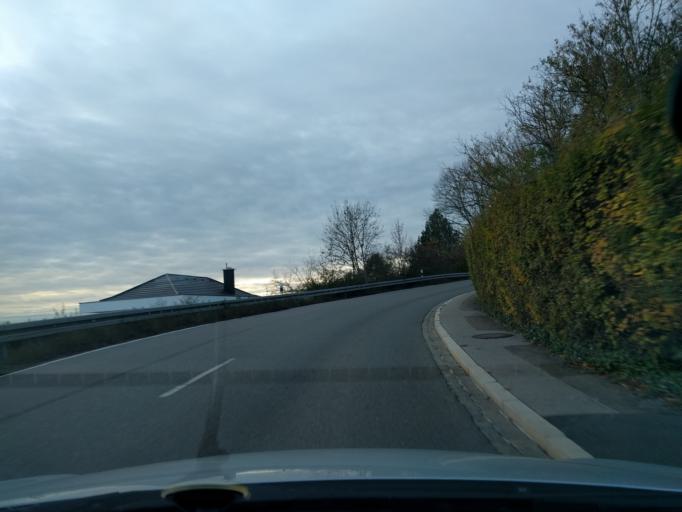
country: DE
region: Bavaria
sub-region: Regierungsbezirk Mittelfranken
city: Herrieden
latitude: 49.2386
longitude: 10.4892
